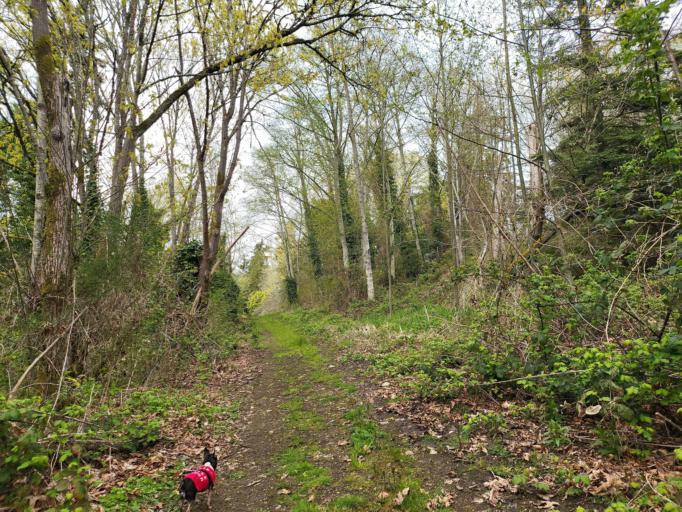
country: US
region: Washington
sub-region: King County
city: Des Moines
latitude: 47.3953
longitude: -122.3141
